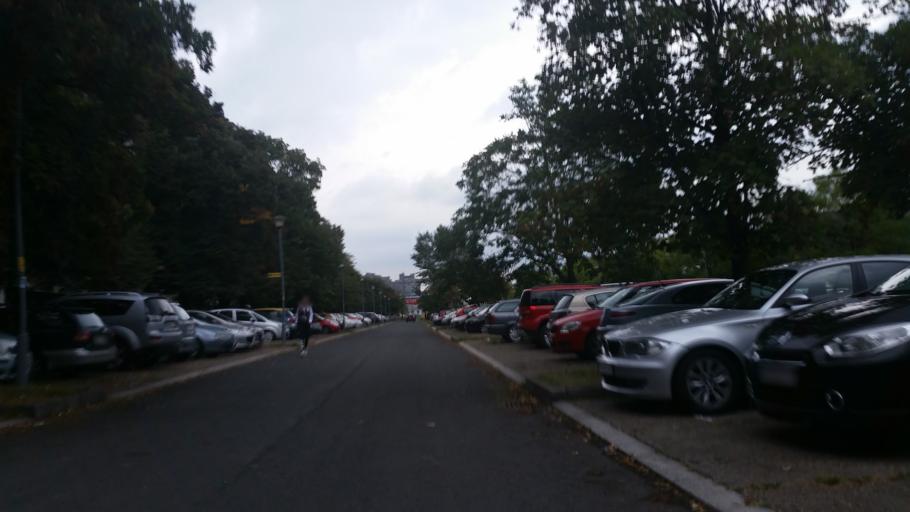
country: RS
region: Central Serbia
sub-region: Belgrade
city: Novi Beograd
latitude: 44.8120
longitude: 20.4130
